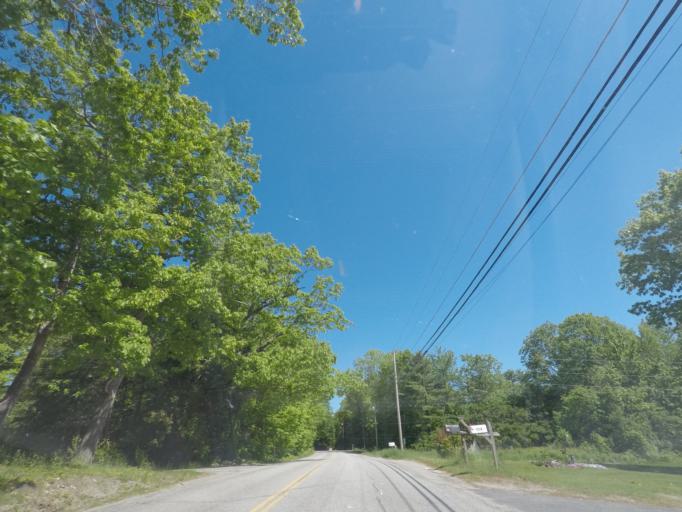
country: US
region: Maine
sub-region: Kennebec County
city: Manchester
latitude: 44.2509
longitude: -69.8999
